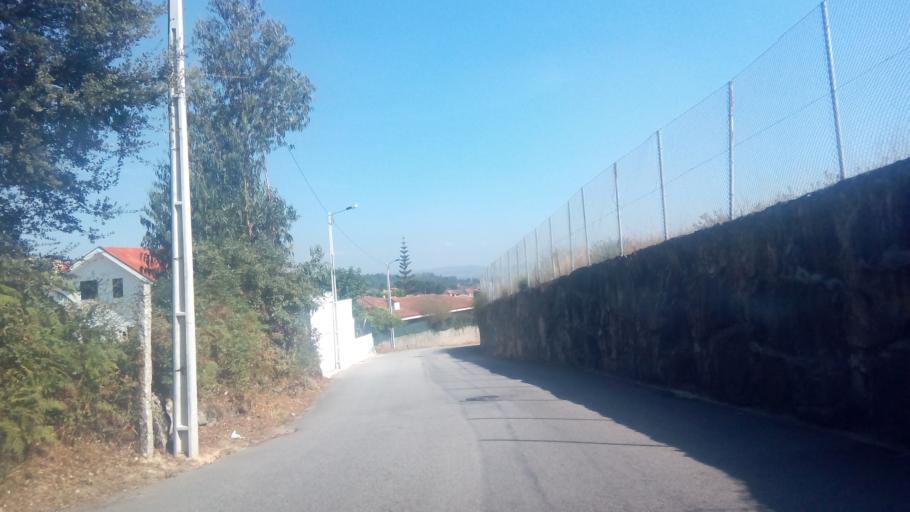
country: PT
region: Porto
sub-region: Paredes
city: Baltar
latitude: 41.1888
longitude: -8.3951
